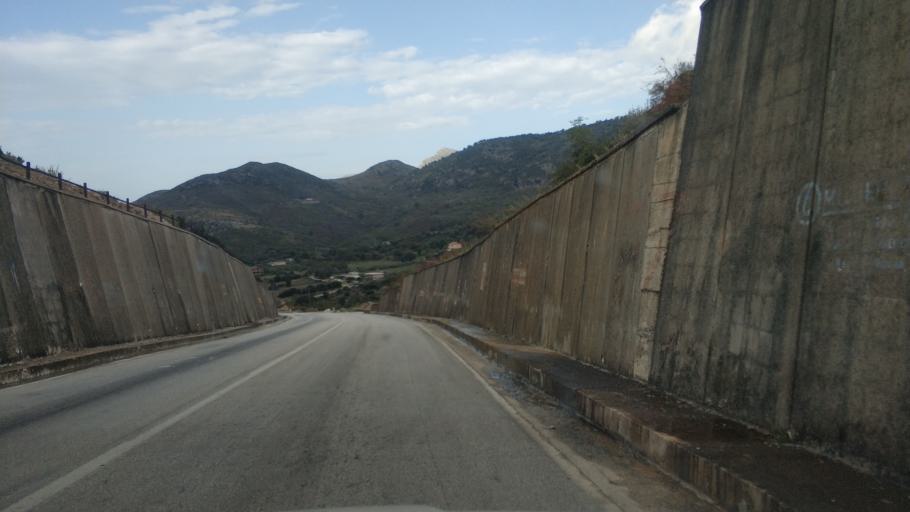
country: AL
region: Vlore
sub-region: Rrethi i Vlores
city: Orikum
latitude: 40.2660
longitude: 19.5160
